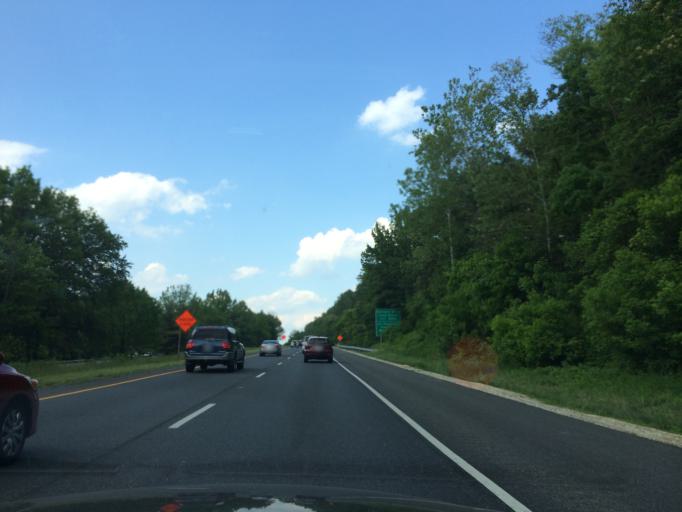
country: US
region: Maryland
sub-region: Howard County
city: Columbia
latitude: 39.2119
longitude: -76.8531
